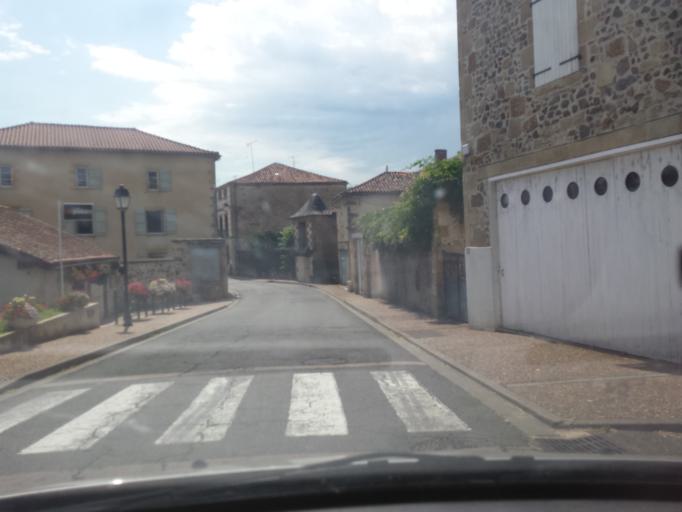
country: FR
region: Poitou-Charentes
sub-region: Departement de la Vienne
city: Availles-Limouzine
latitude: 46.1210
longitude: 0.6563
